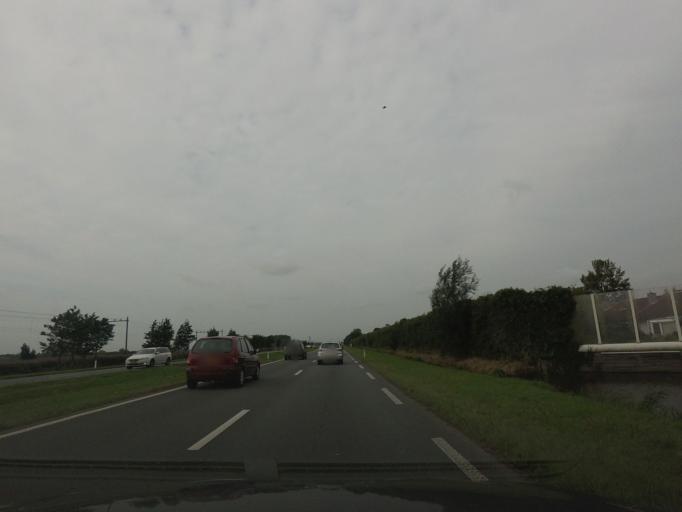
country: NL
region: North Holland
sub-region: Gemeente Uitgeest
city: Uitgeest
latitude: 52.4978
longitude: 4.7481
